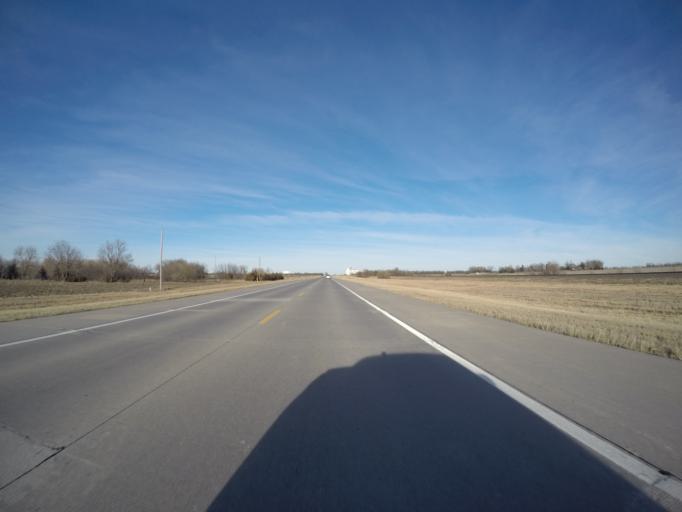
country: US
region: Kansas
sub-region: Harvey County
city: North Newton
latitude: 38.1059
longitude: -97.2699
